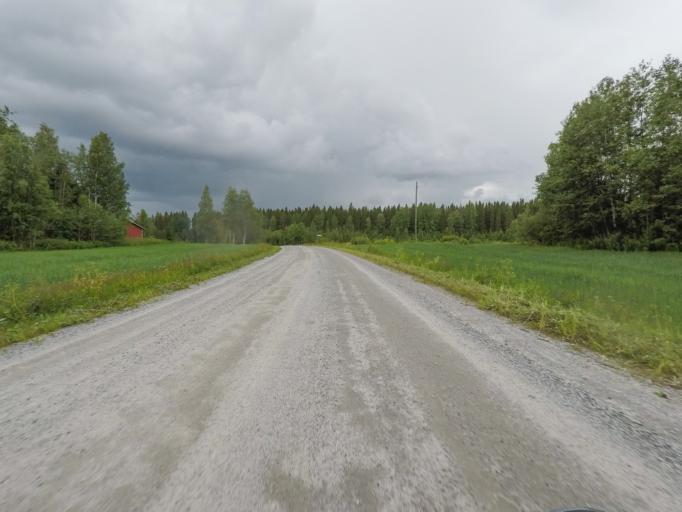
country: FI
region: Central Finland
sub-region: Jyvaeskylae
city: Hankasalmi
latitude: 62.4163
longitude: 26.6179
